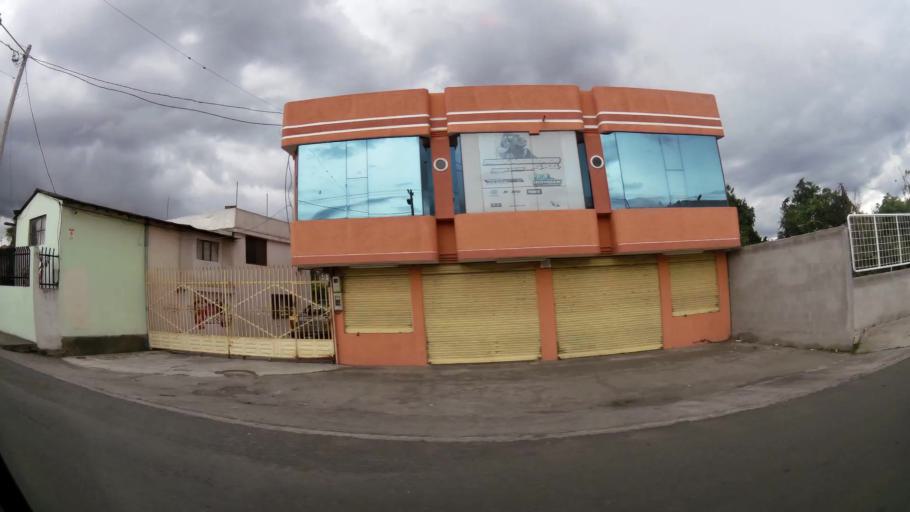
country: EC
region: Tungurahua
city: Ambato
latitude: -1.2763
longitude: -78.6198
